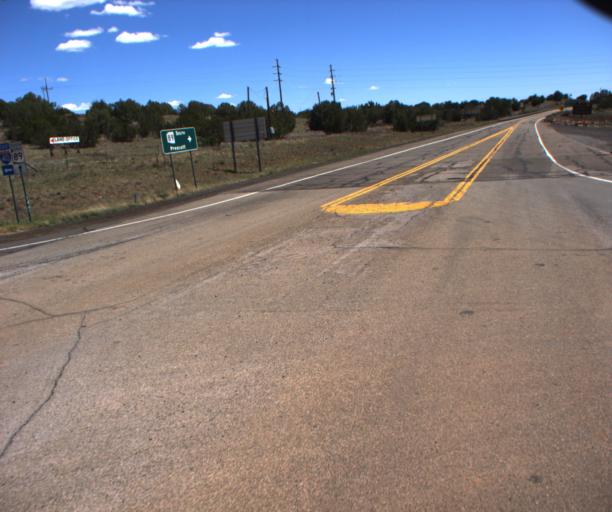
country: US
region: Arizona
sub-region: Coconino County
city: Williams
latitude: 35.2205
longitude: -112.4742
